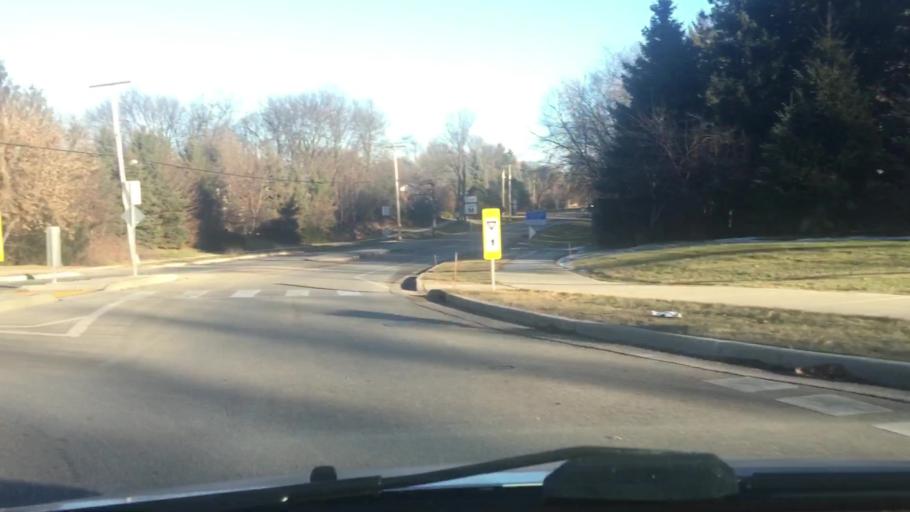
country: US
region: Wisconsin
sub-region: Waukesha County
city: Brookfield
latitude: 43.0612
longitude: -88.1459
